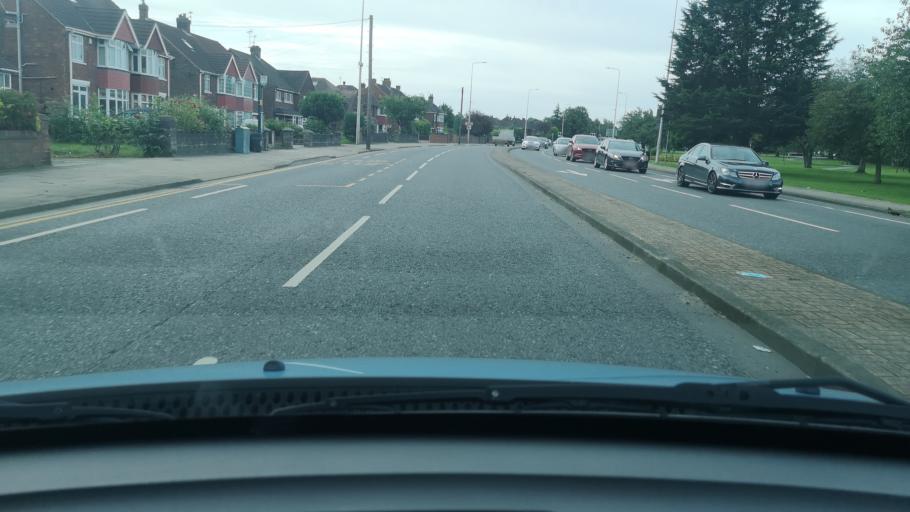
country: GB
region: England
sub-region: North Lincolnshire
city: Scunthorpe
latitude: 53.5838
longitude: -0.6534
